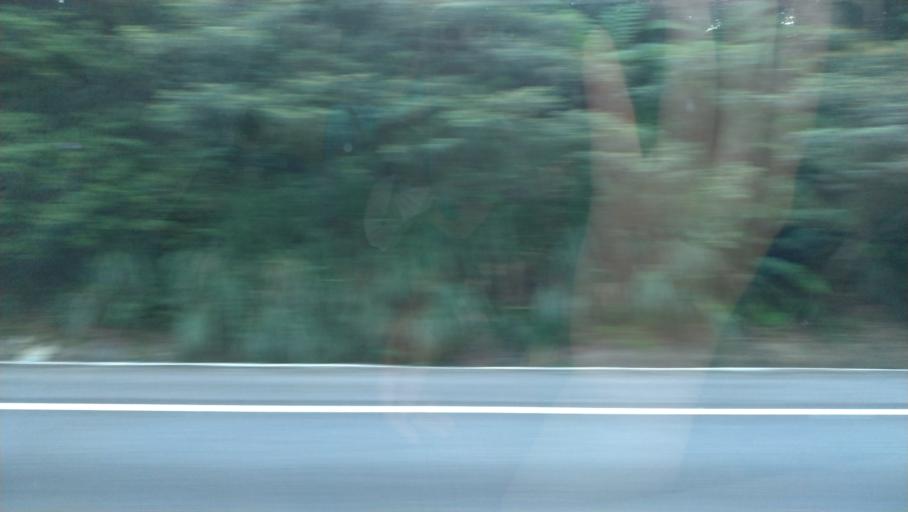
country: TW
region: Taiwan
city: Daxi
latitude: 24.8176
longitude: 121.2004
